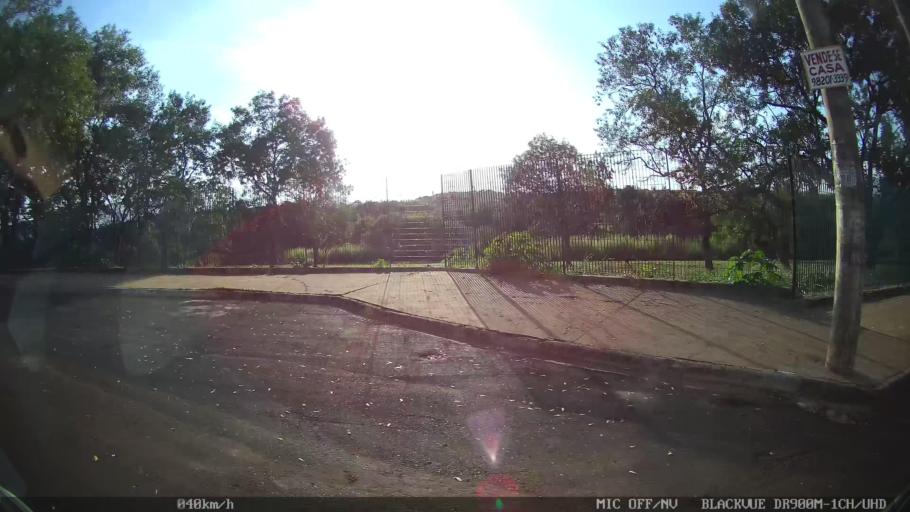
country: BR
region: Sao Paulo
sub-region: Ribeirao Preto
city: Ribeirao Preto
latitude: -21.1500
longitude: -47.8387
